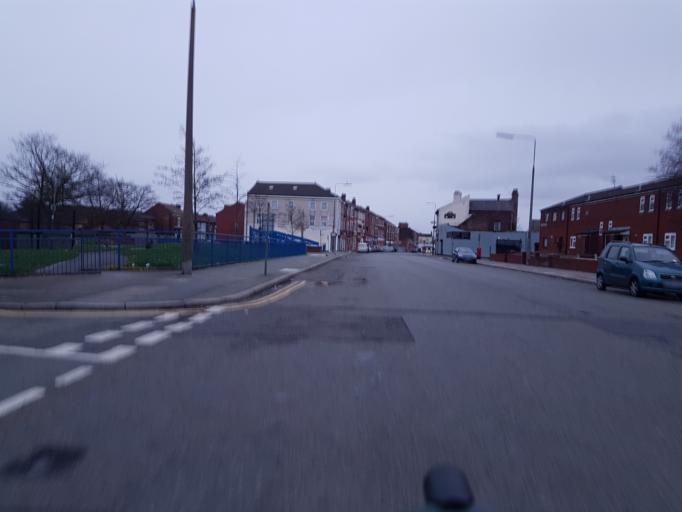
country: GB
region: England
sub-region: Liverpool
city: Liverpool
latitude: 53.4242
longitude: -2.9628
